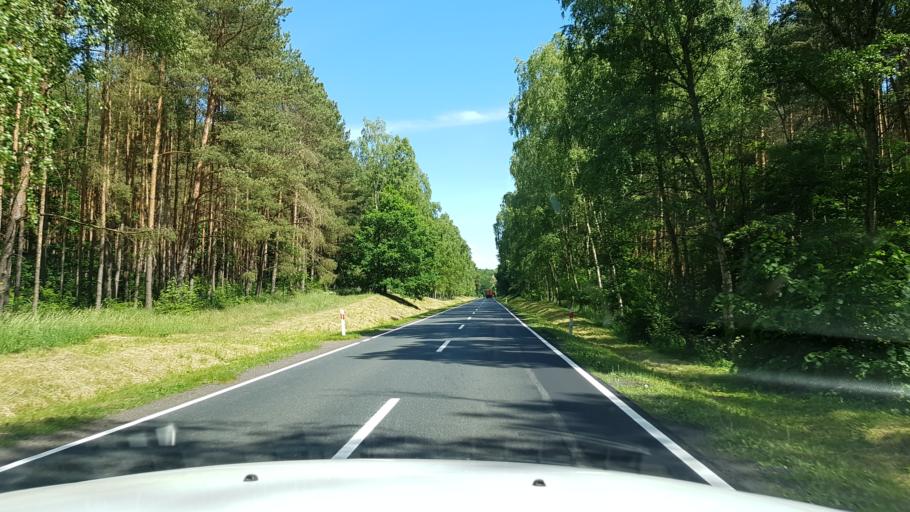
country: PL
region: West Pomeranian Voivodeship
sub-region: Powiat gryfinski
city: Chojna
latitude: 52.9613
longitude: 14.4939
